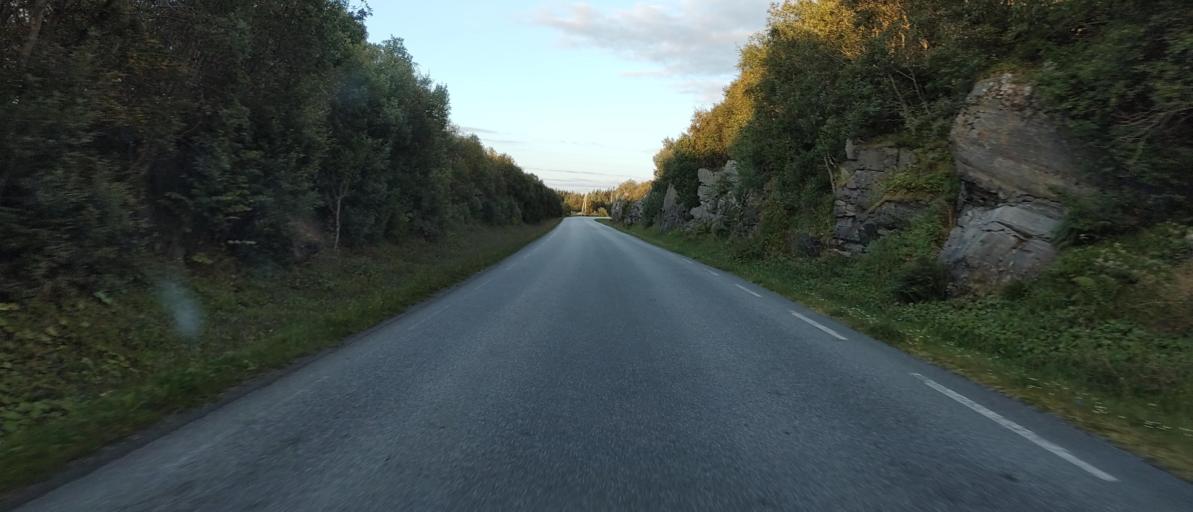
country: NO
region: More og Romsdal
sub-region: Fraena
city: Elnesvagen
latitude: 62.9910
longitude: 7.1861
